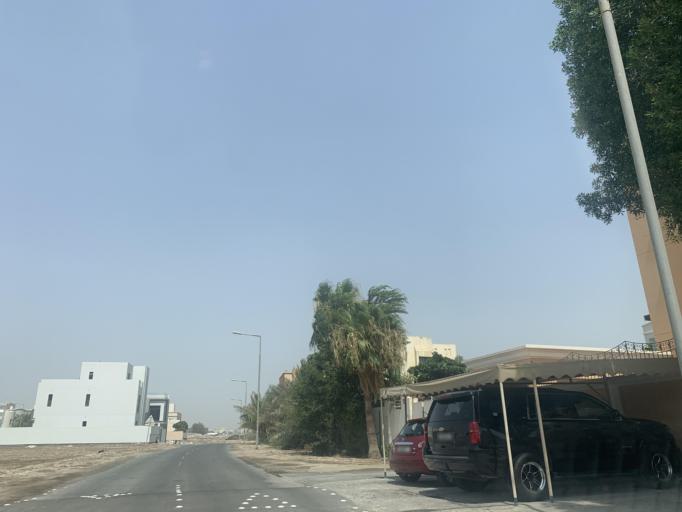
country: BH
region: Northern
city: Madinat `Isa
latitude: 26.1914
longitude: 50.4933
